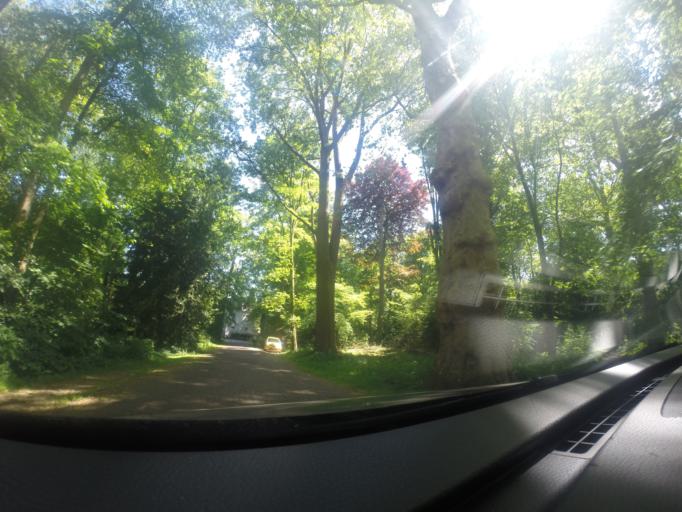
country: NL
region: Gelderland
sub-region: Gemeente Renkum
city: Oosterbeek
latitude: 51.9805
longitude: 5.8322
